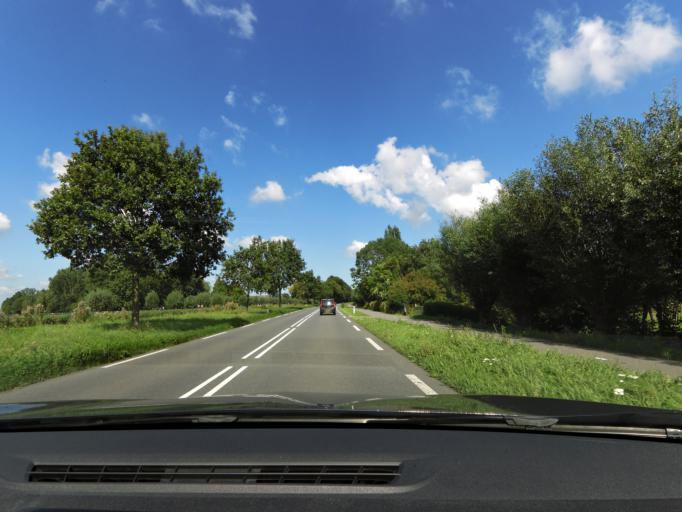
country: NL
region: South Holland
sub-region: Gemeente Alphen aan den Rijn
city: Alphen aan den Rijn
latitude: 52.1582
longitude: 4.7078
